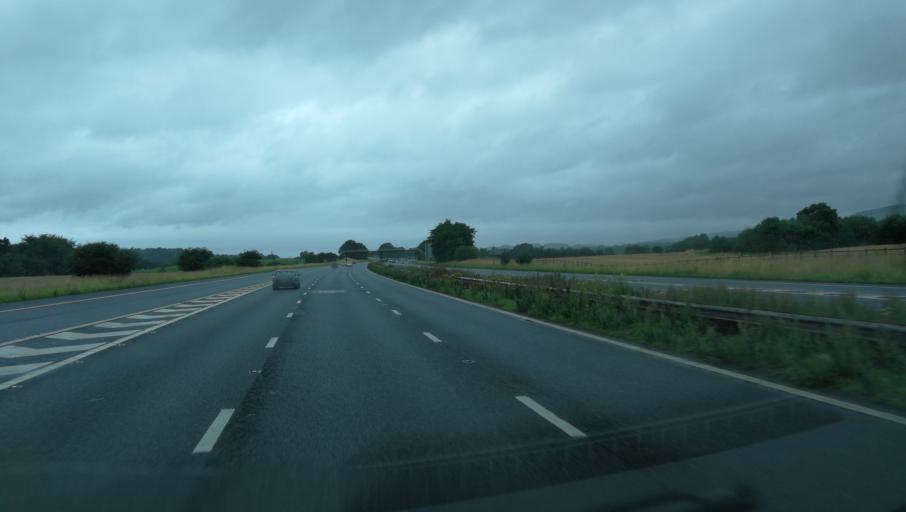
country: GB
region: England
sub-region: Borough of Bolton
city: Horwich
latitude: 53.5769
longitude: -2.5494
